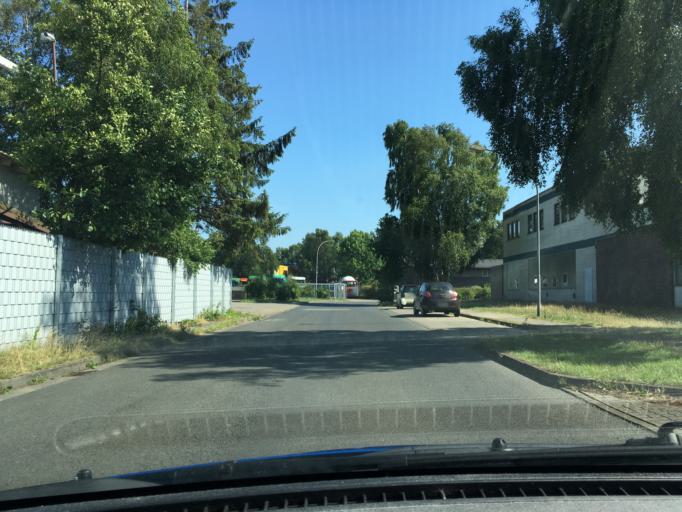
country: DE
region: Hamburg
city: Harburg
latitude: 53.4259
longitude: 10.0416
